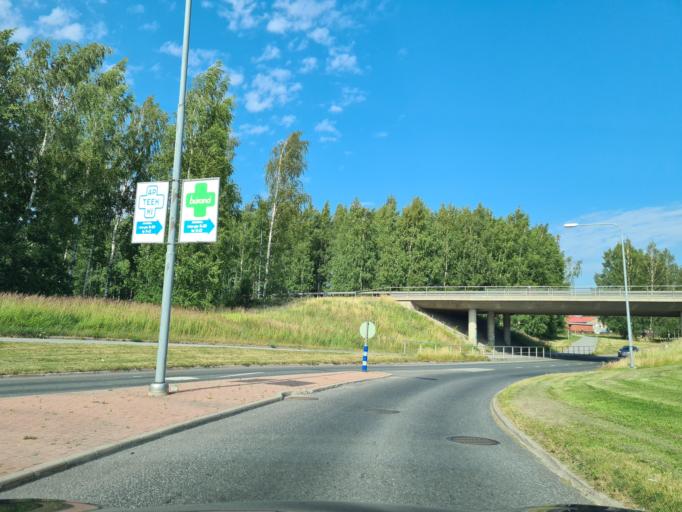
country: FI
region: Satakunta
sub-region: Pori
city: Pori
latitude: 61.4796
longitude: 21.7572
